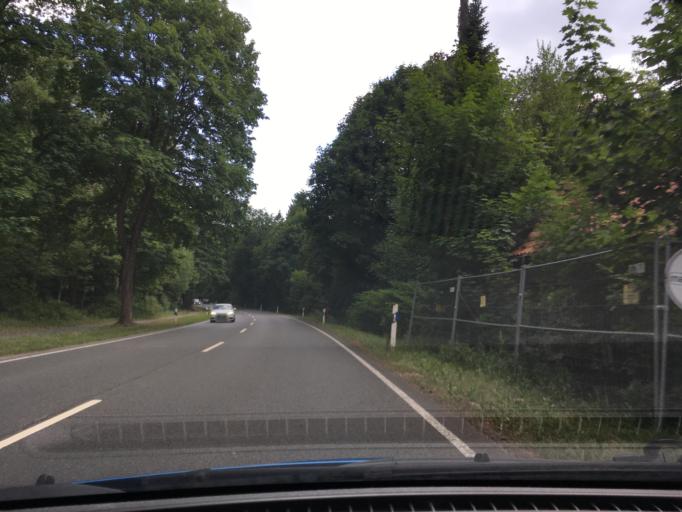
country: DE
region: Lower Saxony
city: Kakenstorf
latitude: 53.2911
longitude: 9.7929
